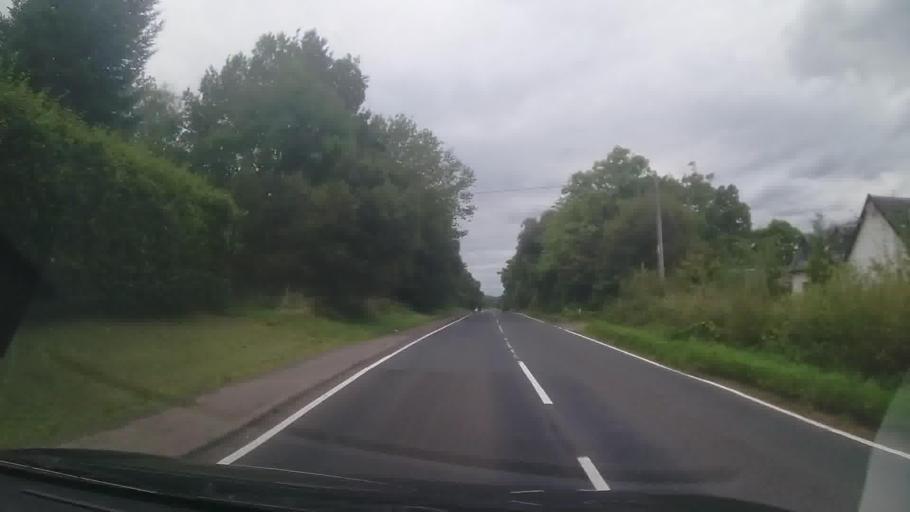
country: GB
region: Scotland
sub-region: Argyll and Bute
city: Garelochhead
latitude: 56.2214
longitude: -5.0341
